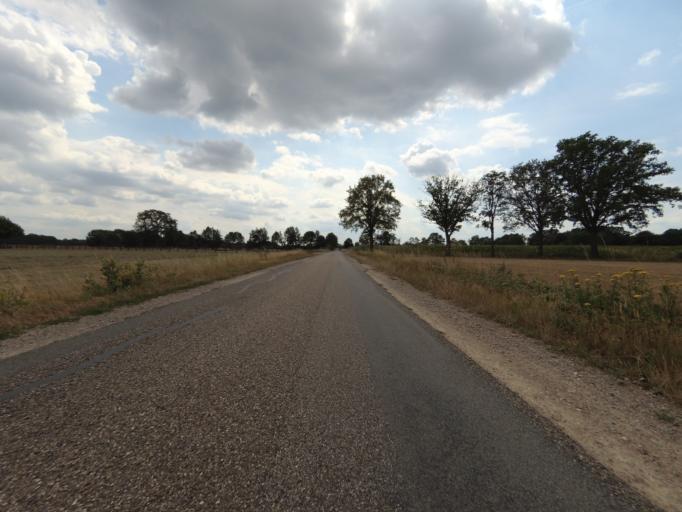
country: NL
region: Gelderland
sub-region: Berkelland
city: Eibergen
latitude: 52.1476
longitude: 6.6737
